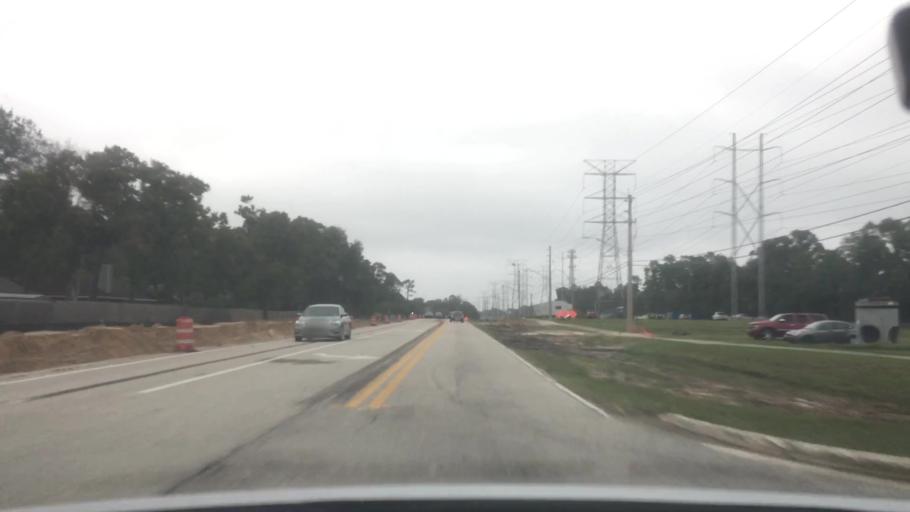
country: US
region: Florida
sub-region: Duval County
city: Atlantic Beach
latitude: 30.3543
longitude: -81.4900
